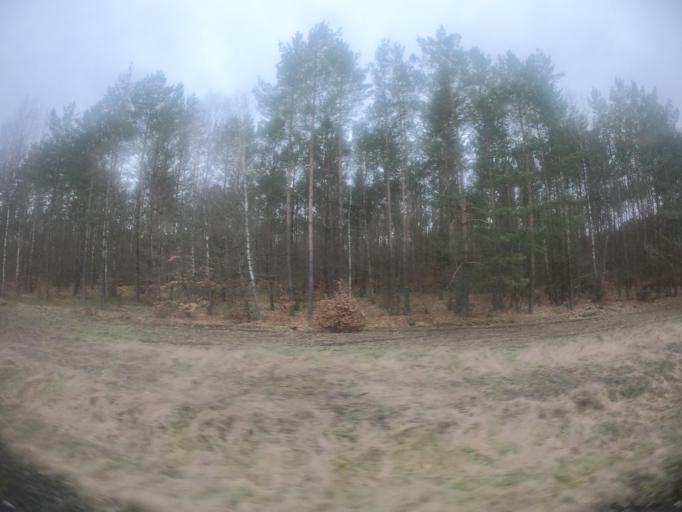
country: PL
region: West Pomeranian Voivodeship
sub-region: Powiat szczecinecki
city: Bialy Bor
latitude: 53.7990
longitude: 16.8641
